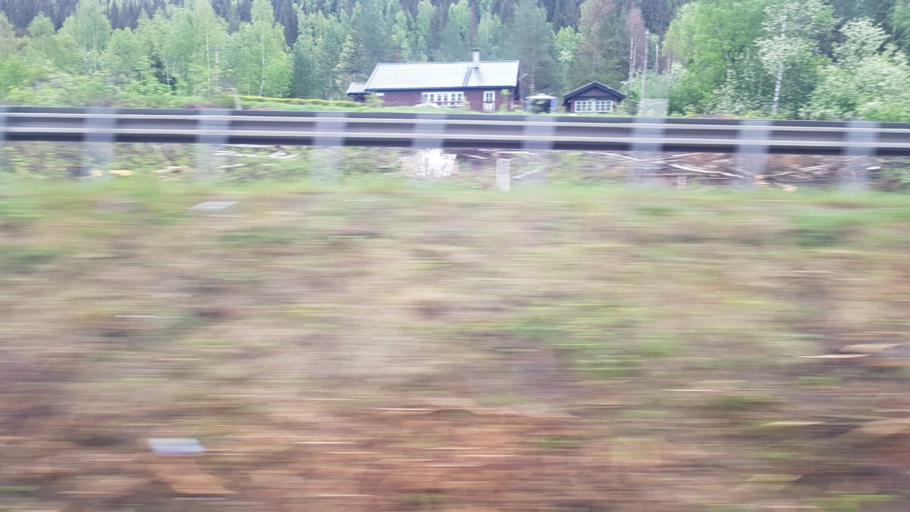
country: NO
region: Oppland
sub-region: Nord-Fron
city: Vinstra
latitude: 61.6238
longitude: 9.7157
